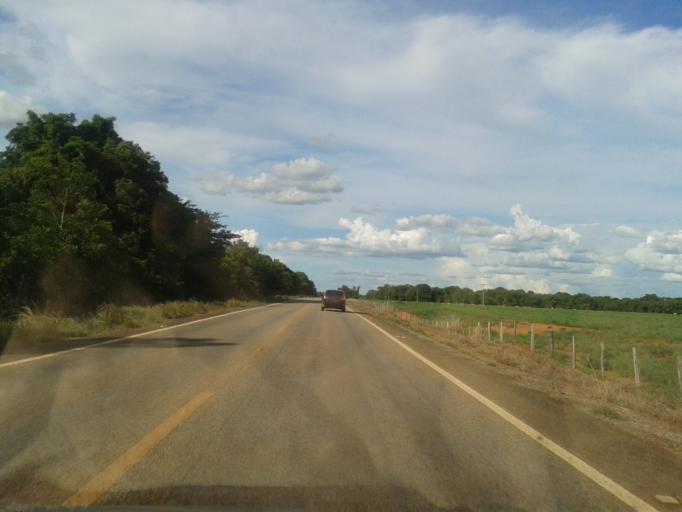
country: BR
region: Goias
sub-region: Mozarlandia
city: Mozarlandia
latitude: -14.3212
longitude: -50.4101
